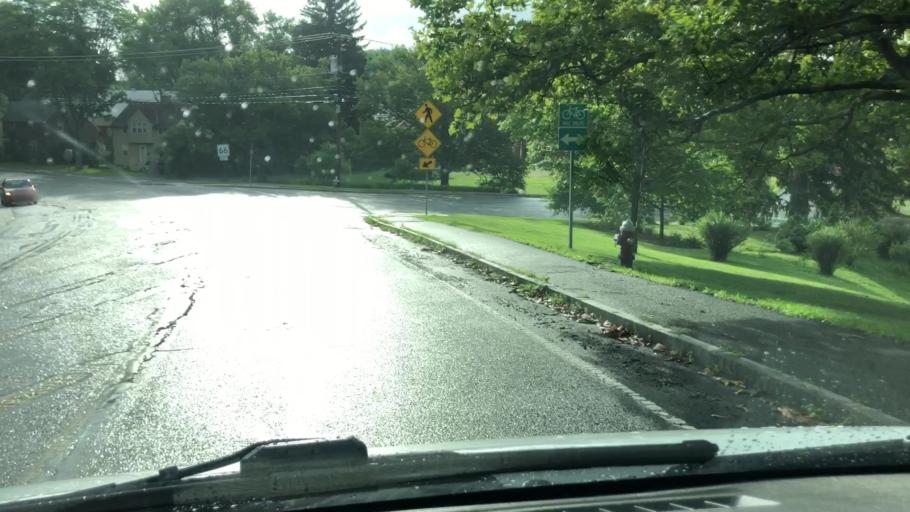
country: US
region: Massachusetts
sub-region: Hampshire County
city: Northampton
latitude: 42.3113
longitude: -72.6439
